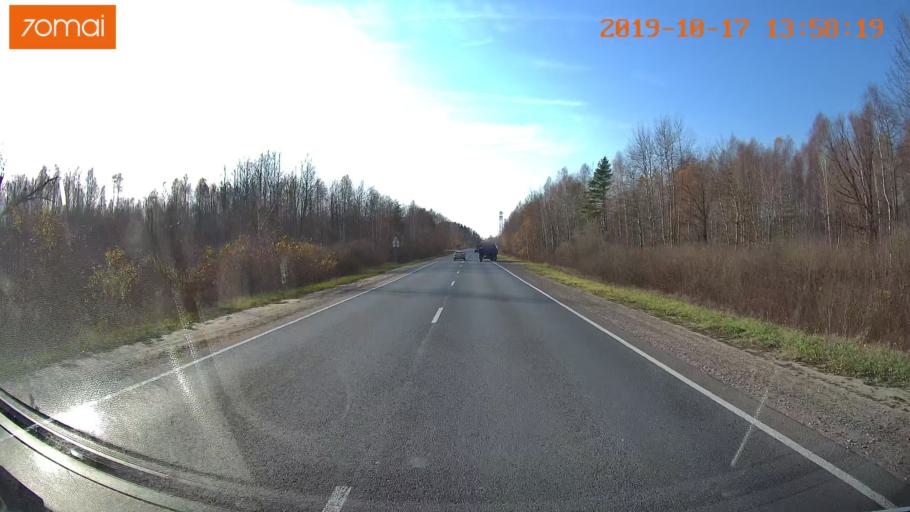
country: RU
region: Rjazan
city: Spas-Klepiki
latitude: 55.1398
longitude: 40.2266
